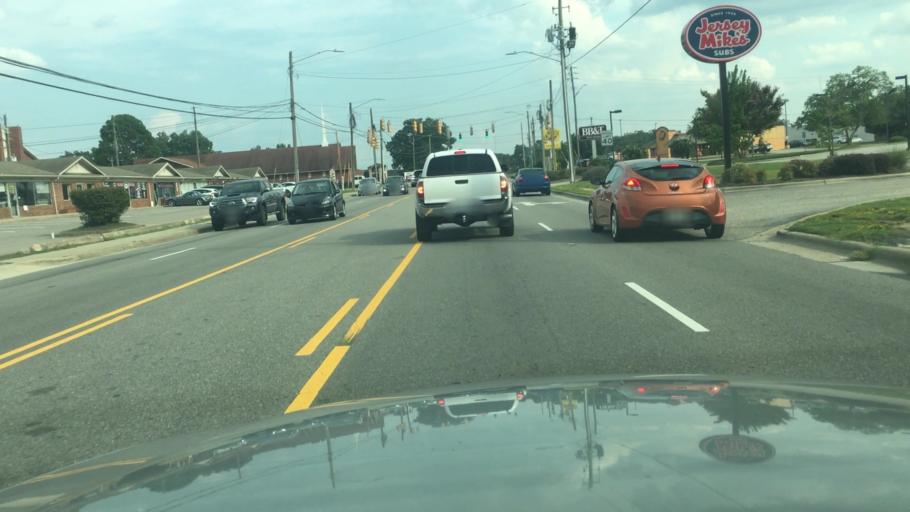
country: US
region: North Carolina
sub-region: Cumberland County
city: Fort Bragg
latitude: 35.0927
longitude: -78.9851
